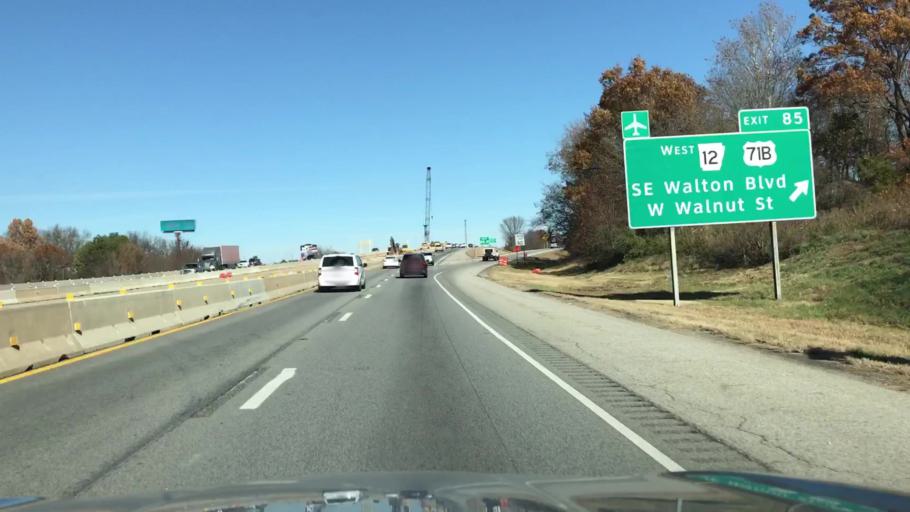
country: US
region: Arkansas
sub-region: Benton County
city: Bentonville
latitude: 36.3310
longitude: -94.1843
